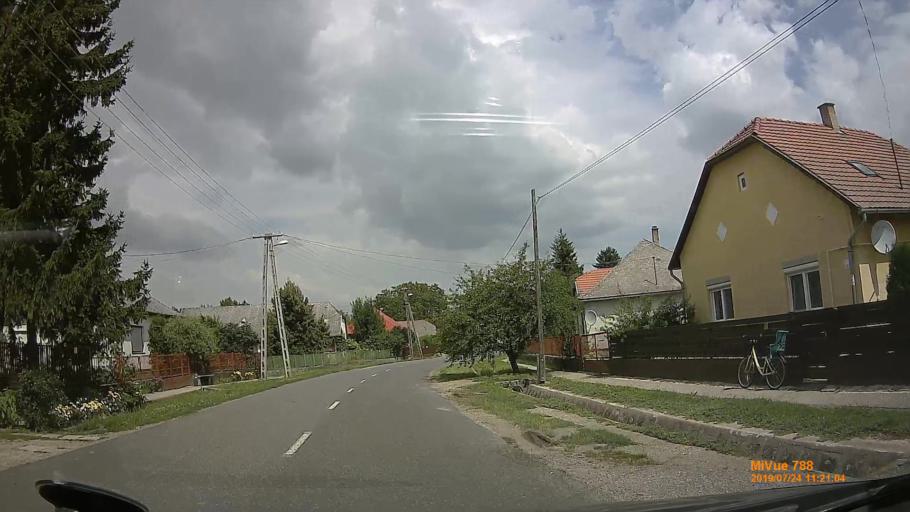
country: HU
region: Szabolcs-Szatmar-Bereg
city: Tarpa
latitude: 48.1630
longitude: 22.4579
